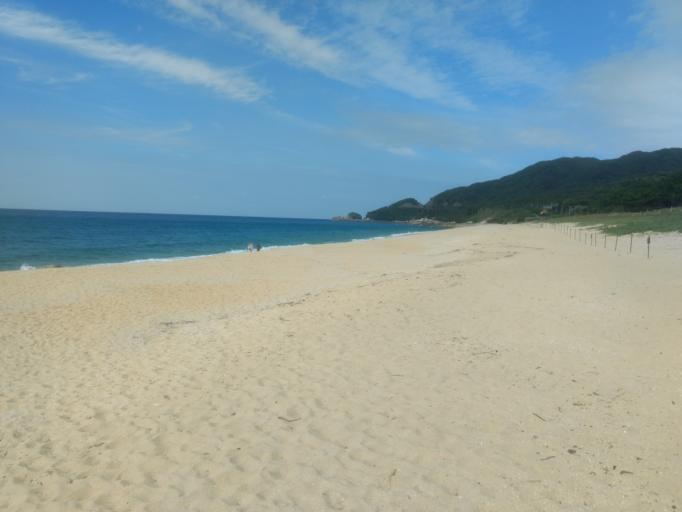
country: JP
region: Kagoshima
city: Nishinoomote
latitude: 30.4068
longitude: 130.4330
